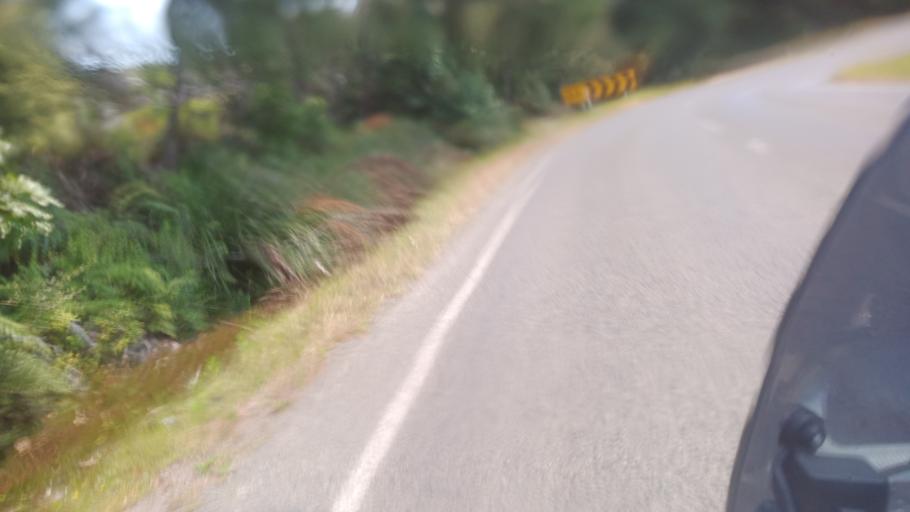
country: NZ
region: Bay of Plenty
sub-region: Opotiki District
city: Opotiki
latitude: -37.5746
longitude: 178.0830
